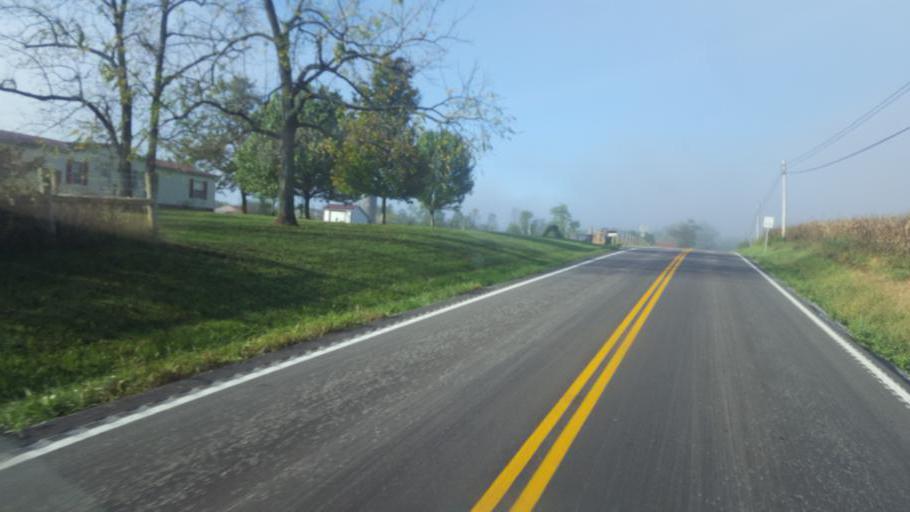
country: US
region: Kentucky
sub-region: Fleming County
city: Flemingsburg
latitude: 38.4809
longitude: -83.6487
